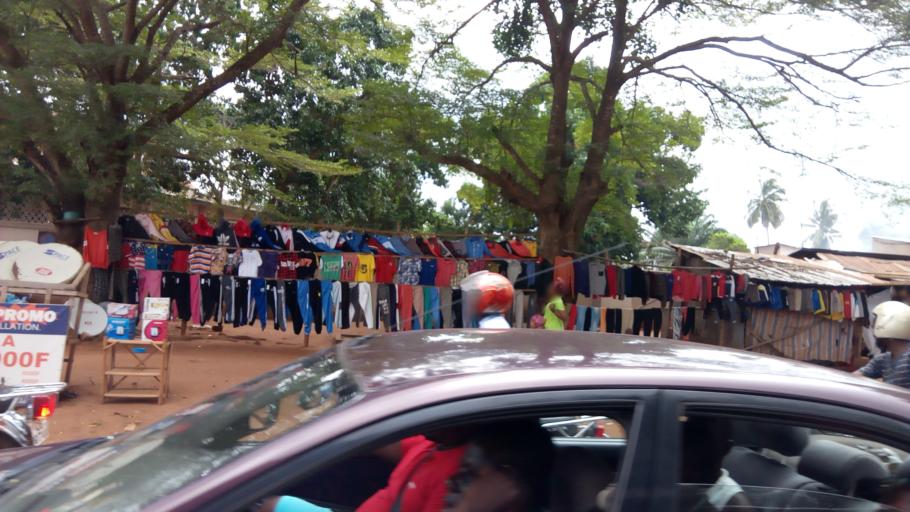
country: TG
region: Maritime
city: Tsevie
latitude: 6.4305
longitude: 1.2128
